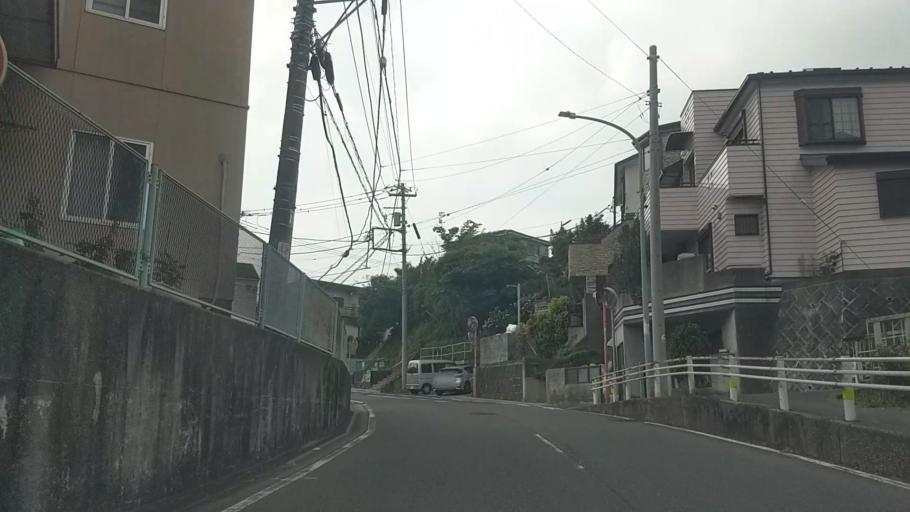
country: JP
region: Kanagawa
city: Kamakura
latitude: 35.3763
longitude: 139.5325
